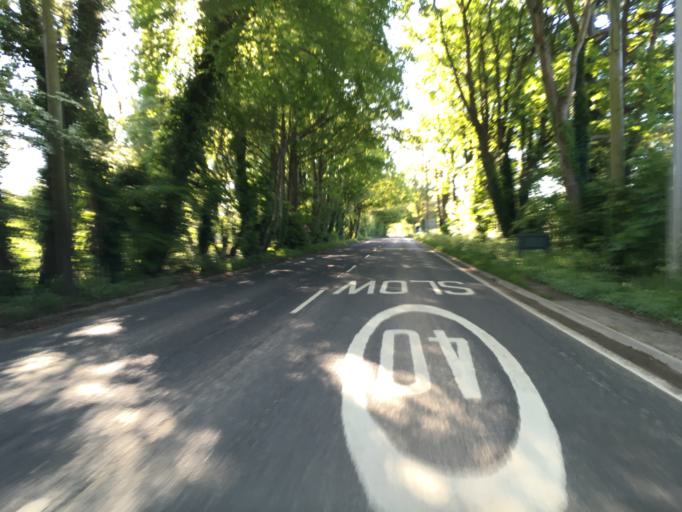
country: GB
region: England
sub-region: North Somerset
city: Long Ashton
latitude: 51.4399
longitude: -2.6823
